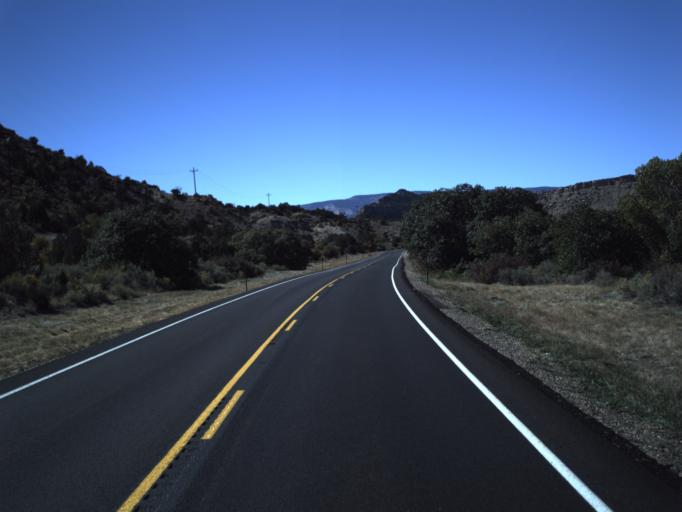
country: US
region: Utah
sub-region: Wayne County
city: Loa
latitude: 37.7724
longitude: -111.6509
